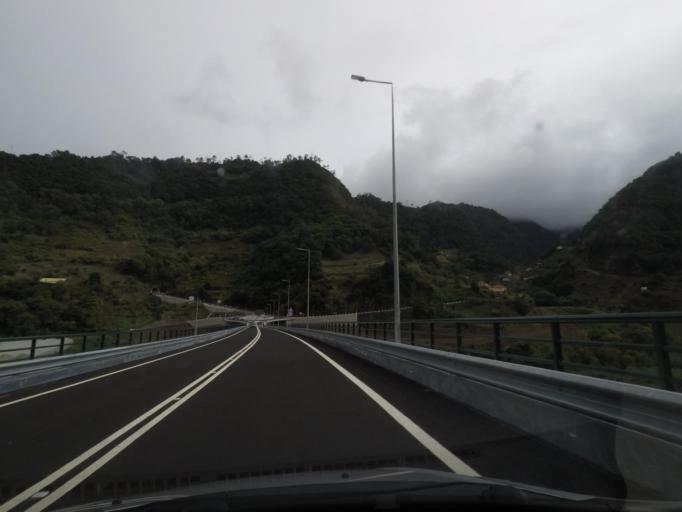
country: PT
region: Madeira
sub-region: Santana
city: Santana
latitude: 32.8171
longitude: -16.9027
